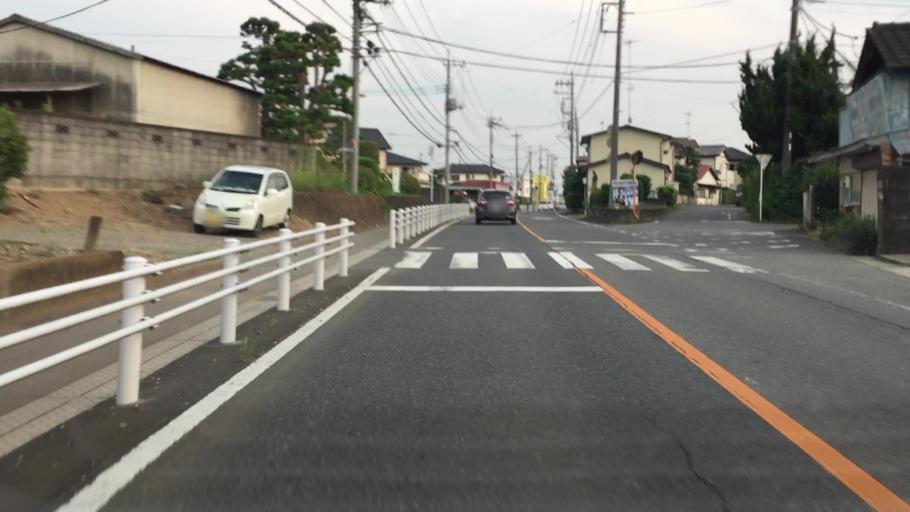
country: JP
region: Tochigi
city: Fujioka
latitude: 36.2684
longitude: 139.6502
